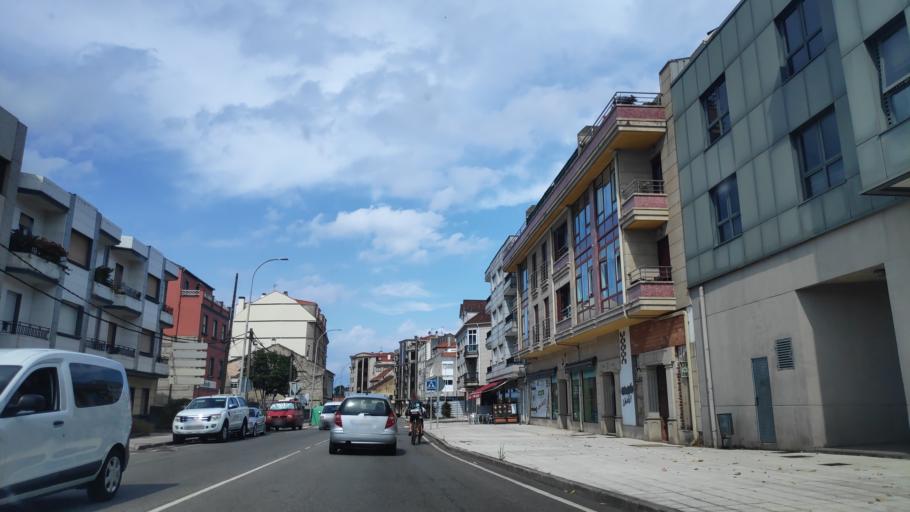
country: ES
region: Galicia
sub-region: Provincia de Pontevedra
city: Vilagarcia de Arousa
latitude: 42.5942
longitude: -8.7522
